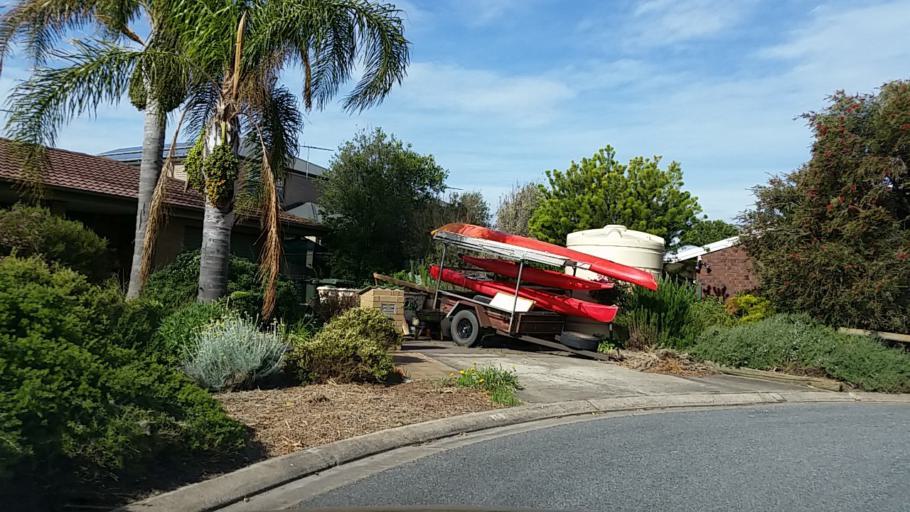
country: AU
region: South Australia
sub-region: Charles Sturt
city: Grange
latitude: -34.8957
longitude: 138.4978
